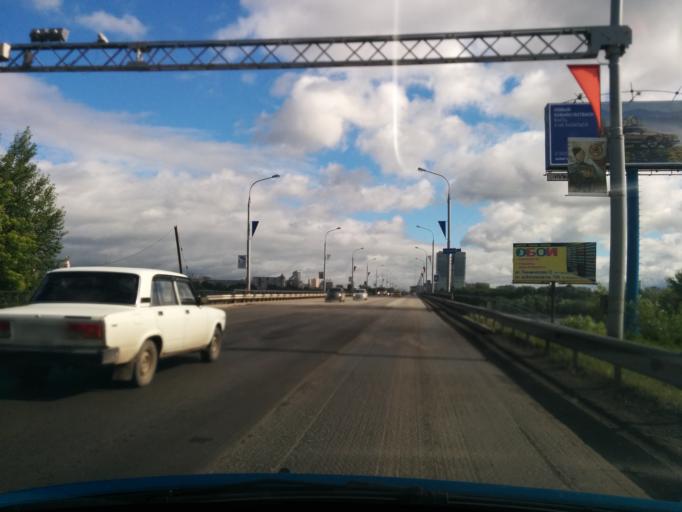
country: RU
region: Perm
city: Perm
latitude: 58.0245
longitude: 56.2192
